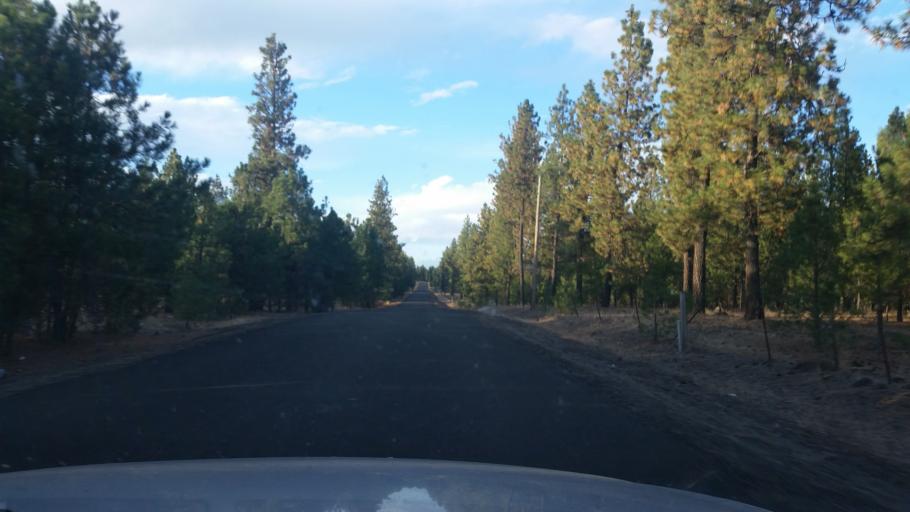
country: US
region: Washington
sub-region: Spokane County
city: Medical Lake
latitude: 47.4415
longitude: -117.7897
